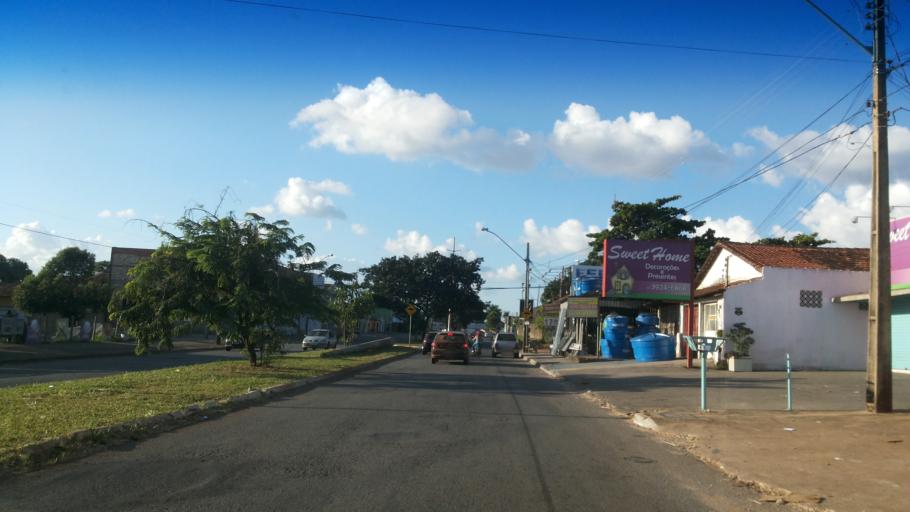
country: BR
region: Goias
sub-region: Goiania
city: Goiania
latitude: -16.7301
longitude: -49.3076
